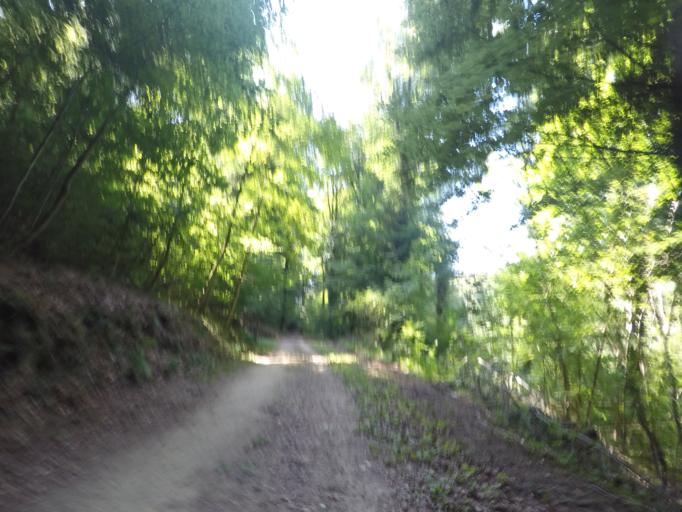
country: LU
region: Luxembourg
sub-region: Canton de Capellen
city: Kopstal
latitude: 49.6485
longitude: 6.0585
